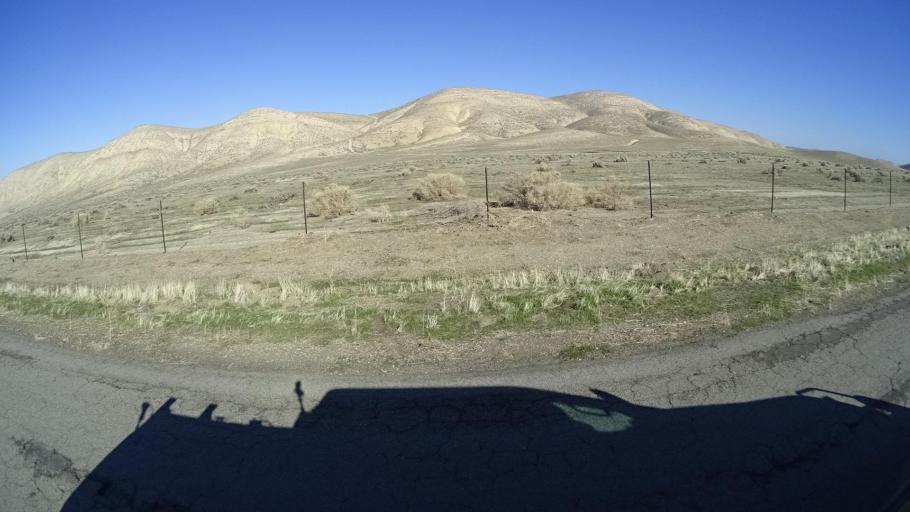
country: US
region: California
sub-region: Kern County
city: Maricopa
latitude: 34.9963
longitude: -119.3970
